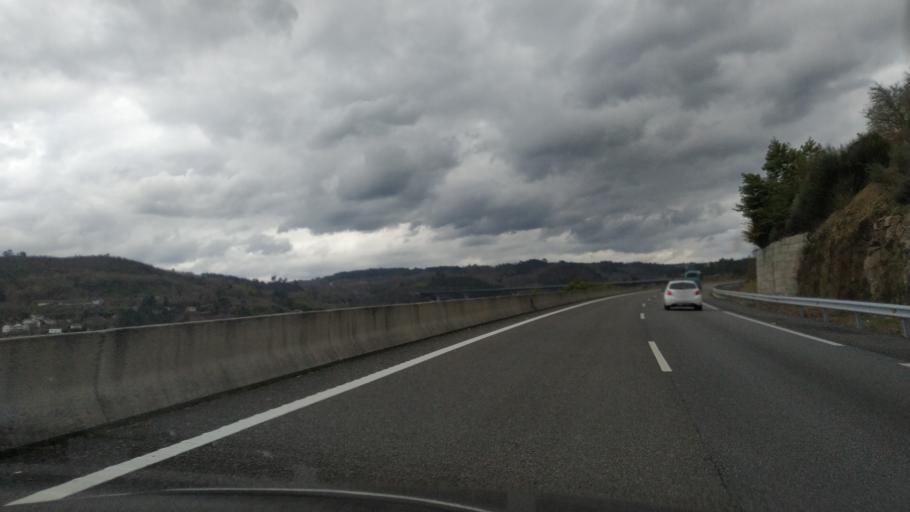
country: ES
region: Galicia
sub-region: Provincia de Ourense
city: Punxin
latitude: 42.3755
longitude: -7.9921
